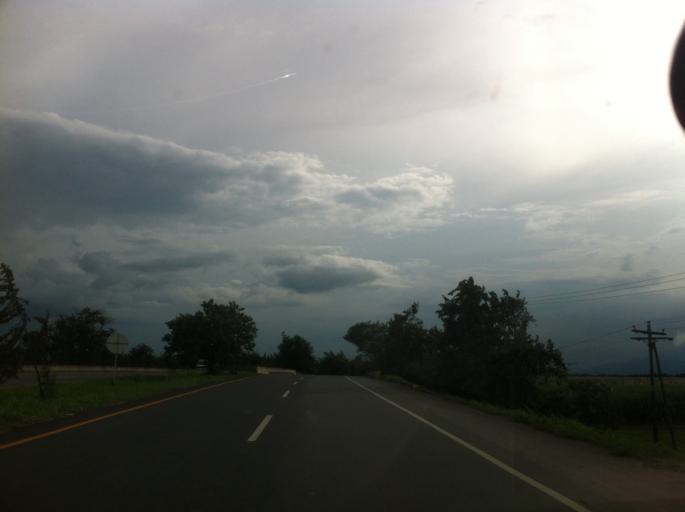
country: CO
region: Valle del Cauca
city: Palmira
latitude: 3.5714
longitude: -76.3308
